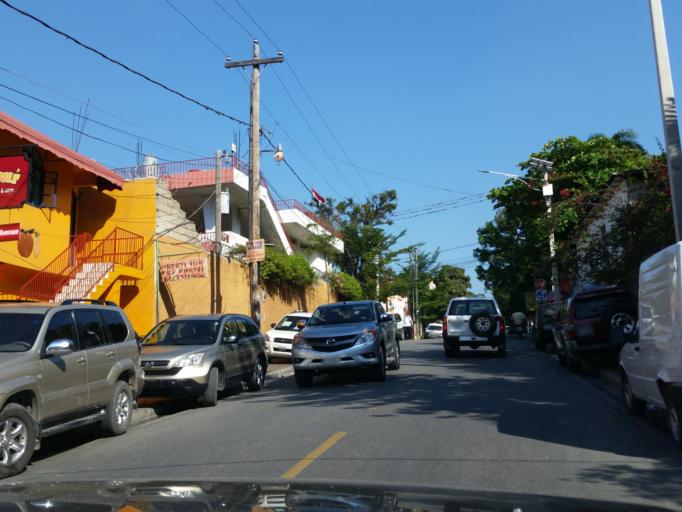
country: HT
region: Ouest
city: Petionville
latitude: 18.5119
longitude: -72.2892
